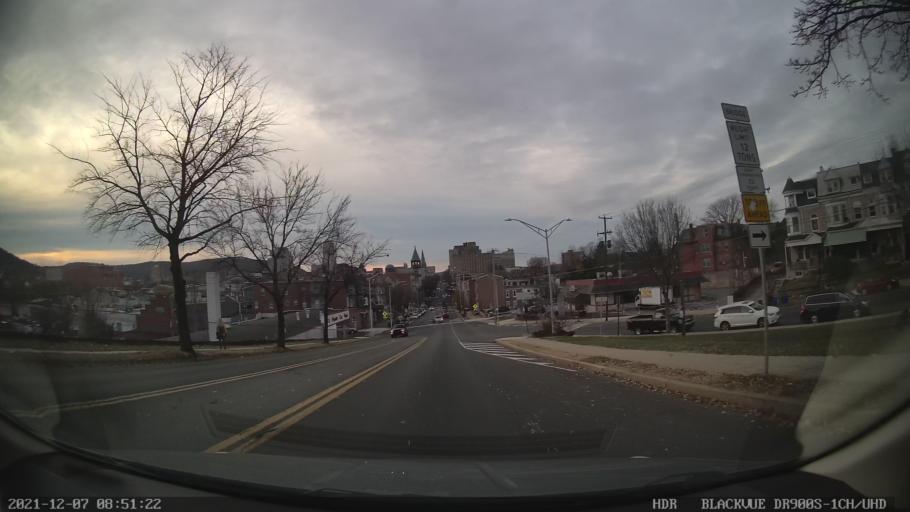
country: US
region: Pennsylvania
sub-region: Berks County
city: Reading
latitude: 40.3434
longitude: -75.9278
